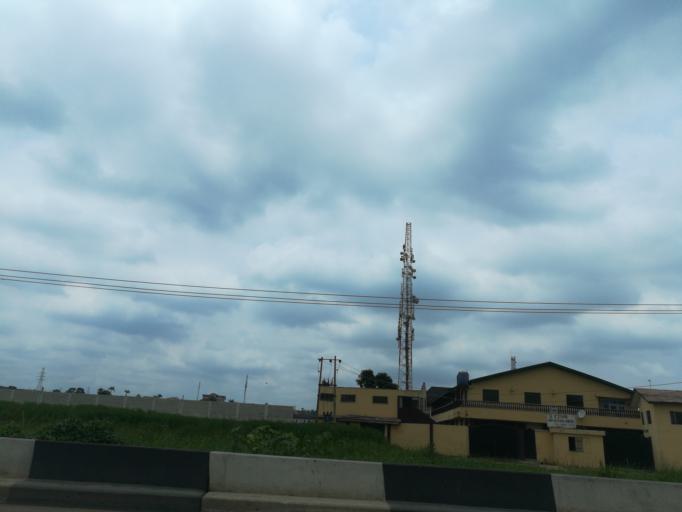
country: NG
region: Lagos
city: Ojota
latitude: 6.5835
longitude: 3.3910
